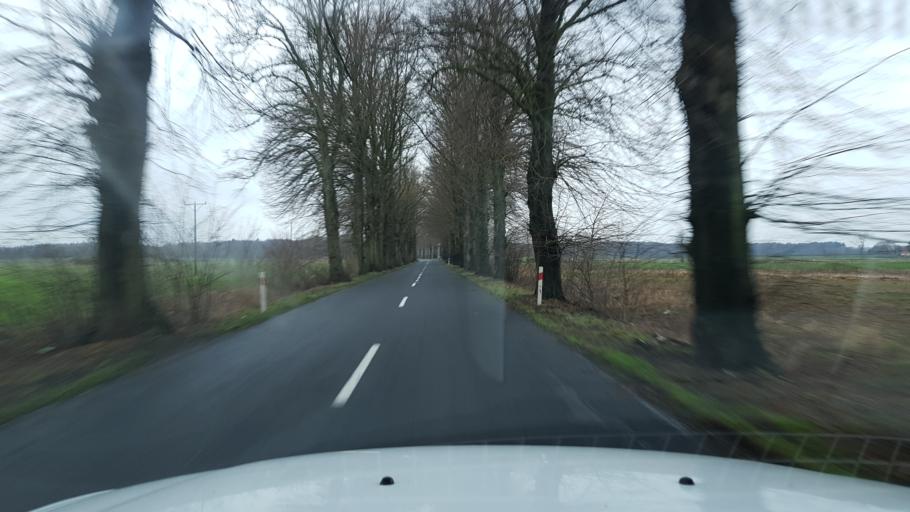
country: PL
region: West Pomeranian Voivodeship
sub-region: Powiat gryficki
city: Brojce
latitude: 54.0586
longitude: 15.3783
